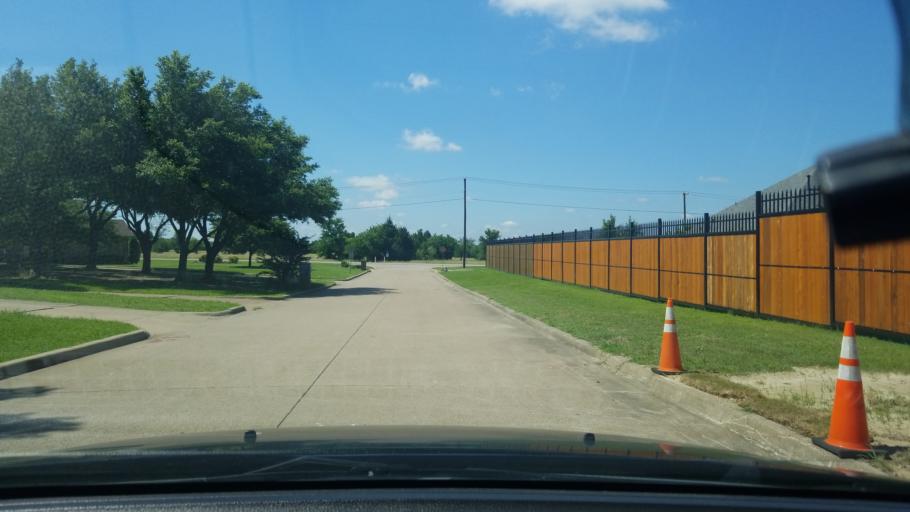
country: US
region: Texas
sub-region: Dallas County
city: Sunnyvale
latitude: 32.7972
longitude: -96.5891
